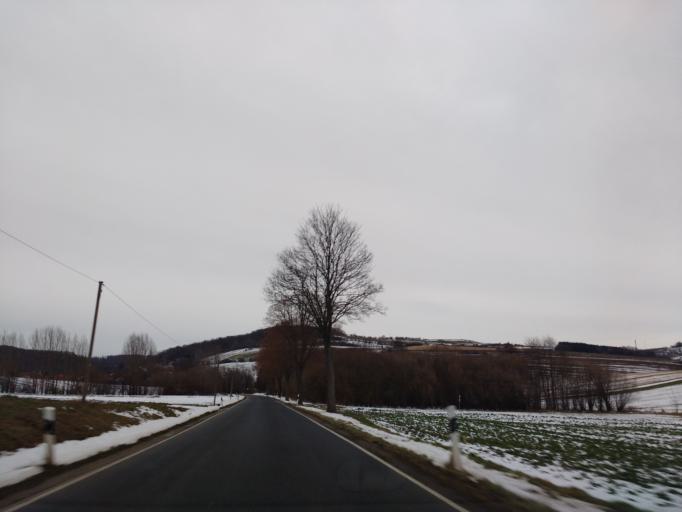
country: DE
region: Thuringia
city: Arenshausen
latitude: 51.4015
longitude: 9.9622
